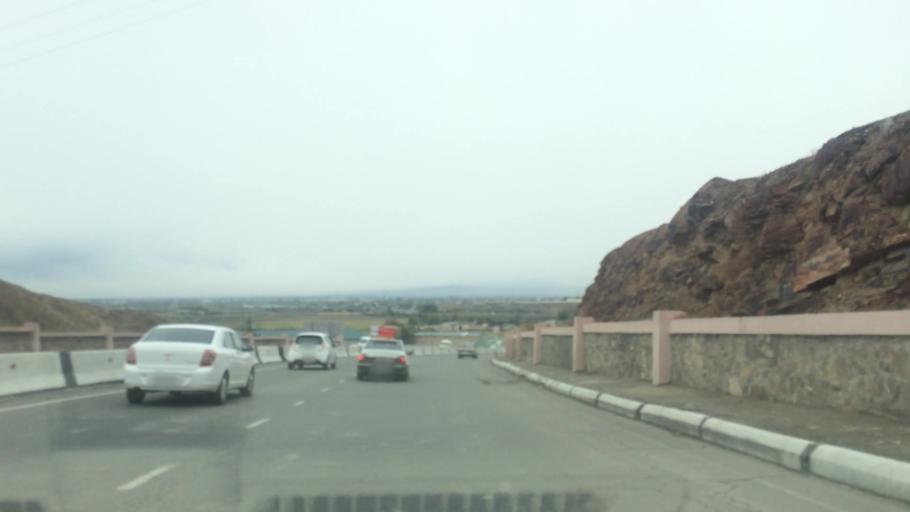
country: UZ
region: Samarqand
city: Jomboy
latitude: 39.6846
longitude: 67.0517
